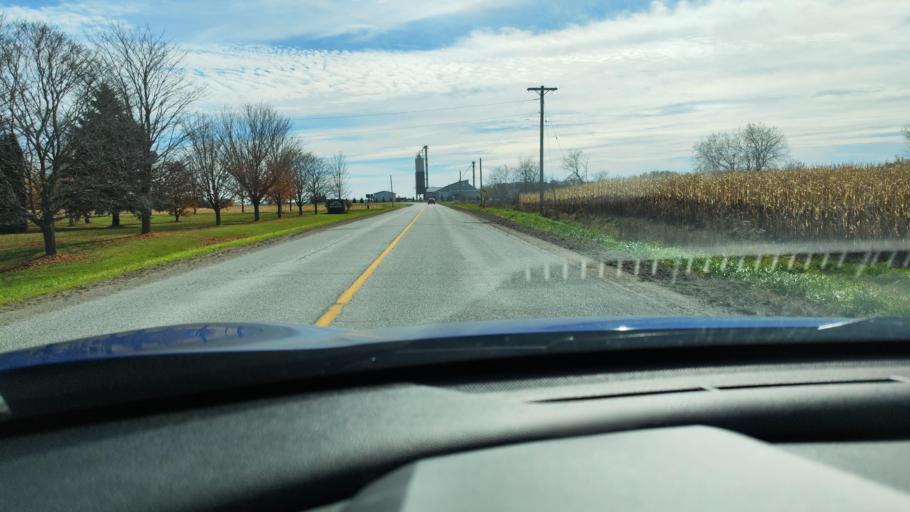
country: CA
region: Ontario
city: Wasaga Beach
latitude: 44.4422
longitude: -79.9990
